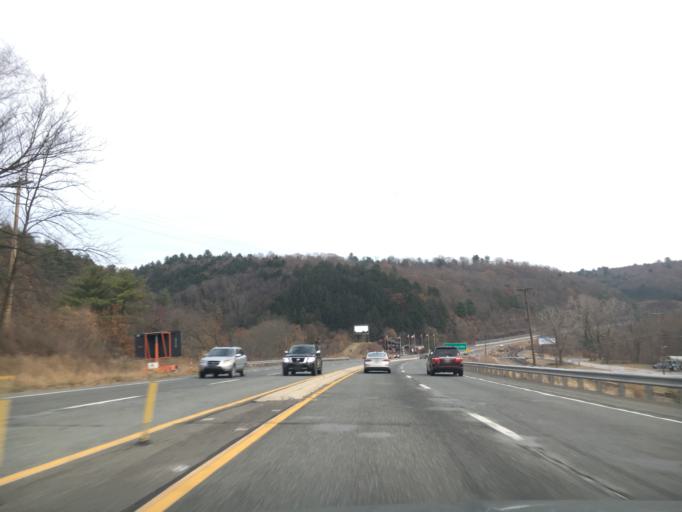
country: US
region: Pennsylvania
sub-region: Carbon County
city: Weissport East
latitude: 40.8179
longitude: -75.6759
